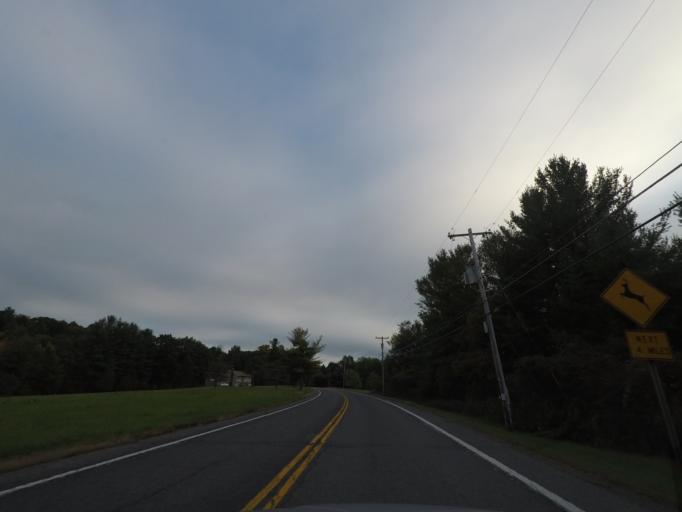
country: US
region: New York
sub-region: Rensselaer County
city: Nassau
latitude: 42.5794
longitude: -73.6255
